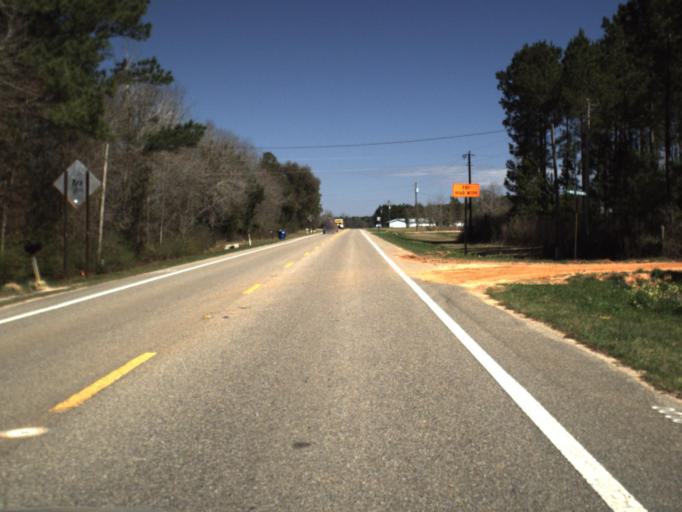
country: US
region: Florida
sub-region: Calhoun County
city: Blountstown
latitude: 30.5013
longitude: -85.0400
